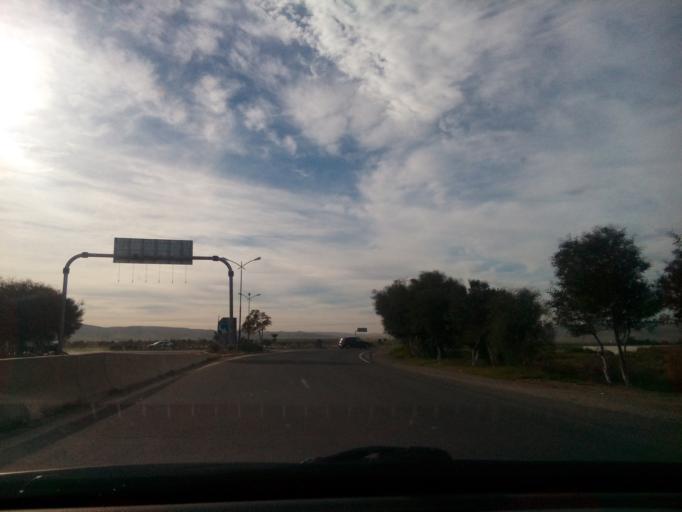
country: DZ
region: Mascara
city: Sig
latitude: 35.5372
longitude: -0.3781
